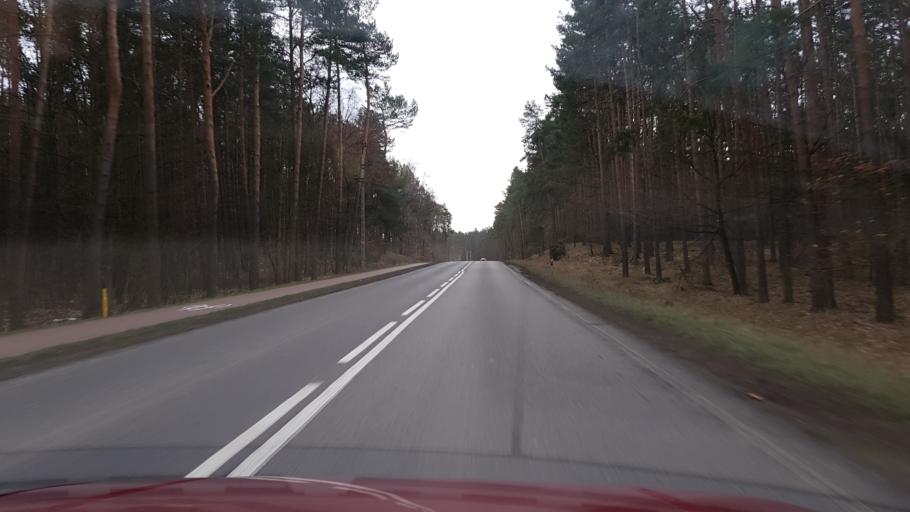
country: PL
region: West Pomeranian Voivodeship
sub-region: Powiat policki
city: Dobra
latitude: 53.5241
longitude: 14.4693
